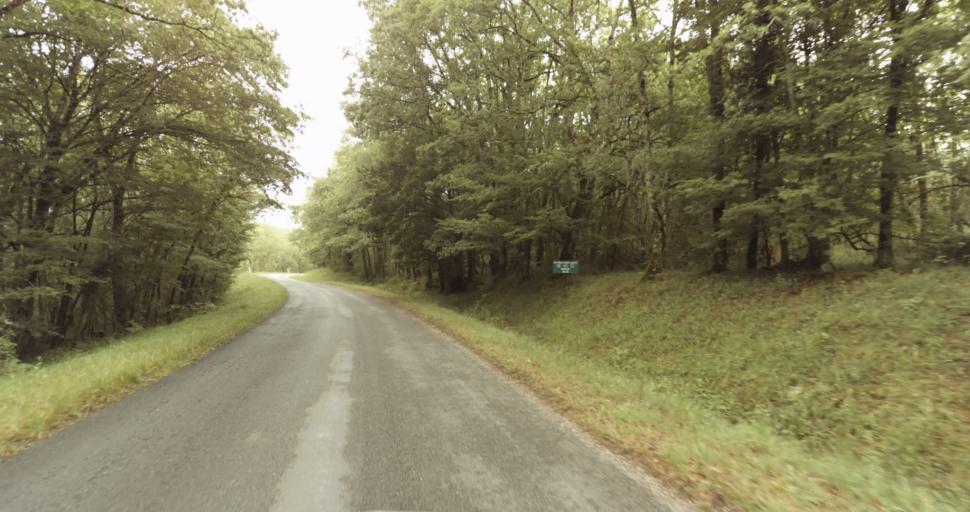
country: FR
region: Aquitaine
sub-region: Departement de la Dordogne
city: Lalinde
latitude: 44.8949
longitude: 0.7702
